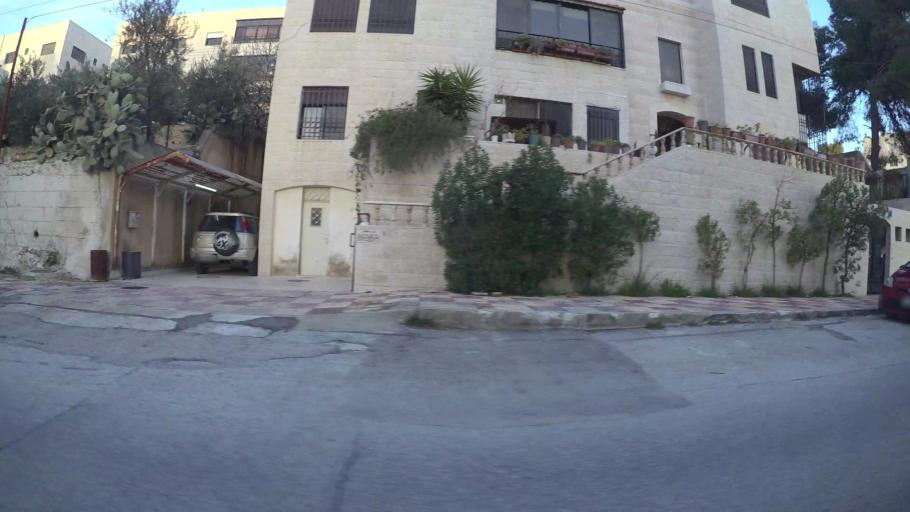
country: JO
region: Amman
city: Al Jubayhah
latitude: 31.9958
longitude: 35.8612
